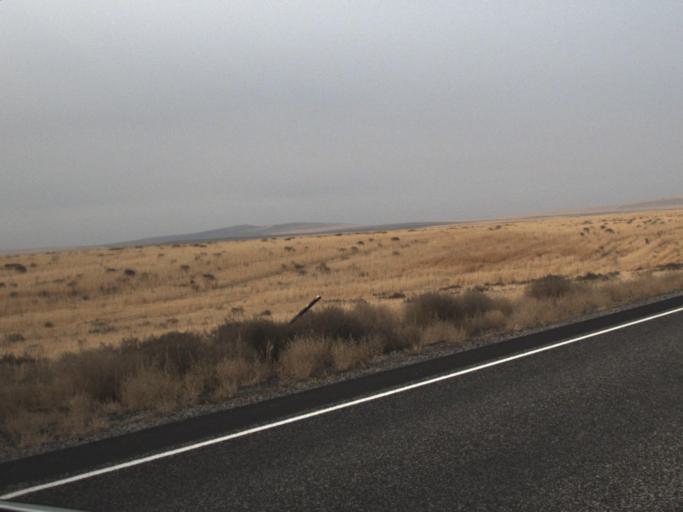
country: US
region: Washington
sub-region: Benton County
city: Benton City
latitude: 46.1413
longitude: -119.6011
